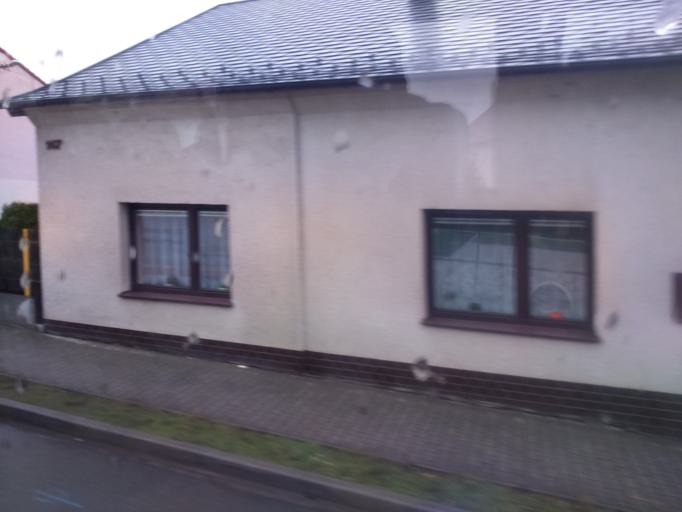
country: CZ
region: Plzensky
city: Line
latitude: 49.6962
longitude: 13.2594
